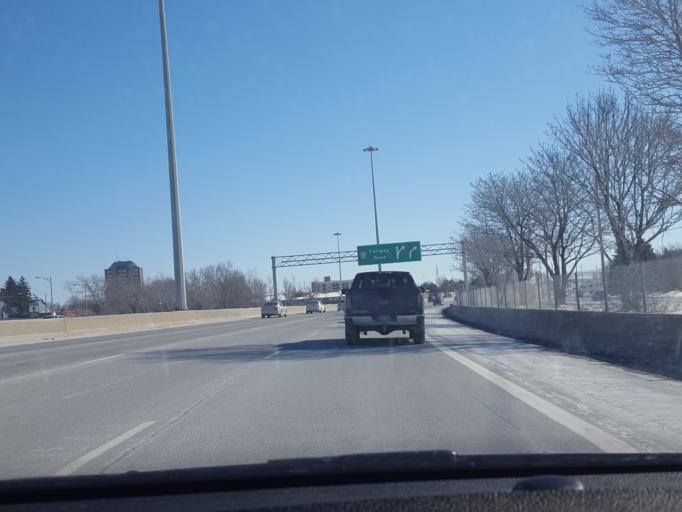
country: CA
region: Ontario
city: Kitchener
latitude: 43.4312
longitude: -80.4416
